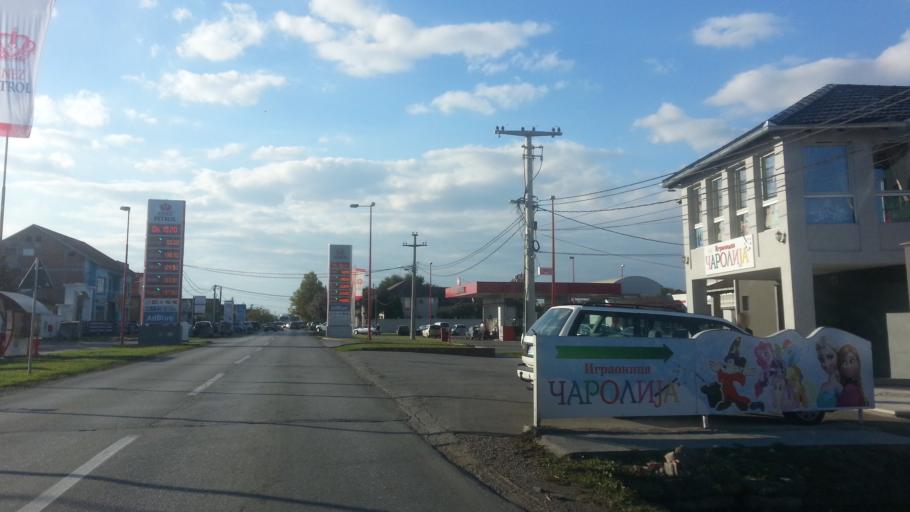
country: RS
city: Novi Banovci
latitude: 44.9126
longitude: 20.2635
